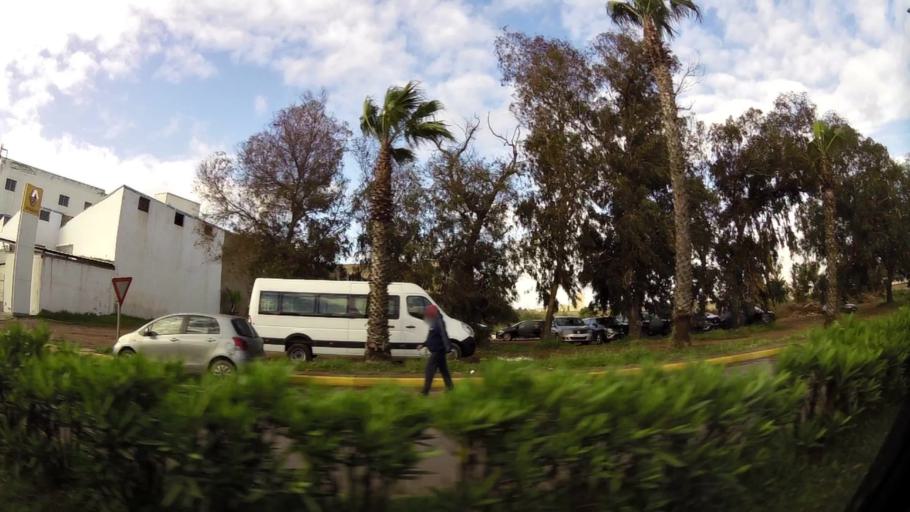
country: MA
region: Grand Casablanca
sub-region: Mohammedia
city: Mohammedia
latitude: 33.6829
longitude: -7.4090
